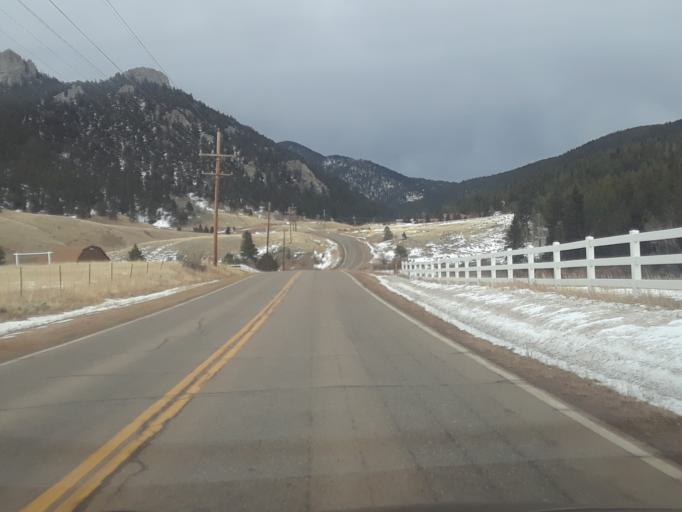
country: US
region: Colorado
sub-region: Gilpin County
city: Central City
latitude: 39.8383
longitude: -105.4404
